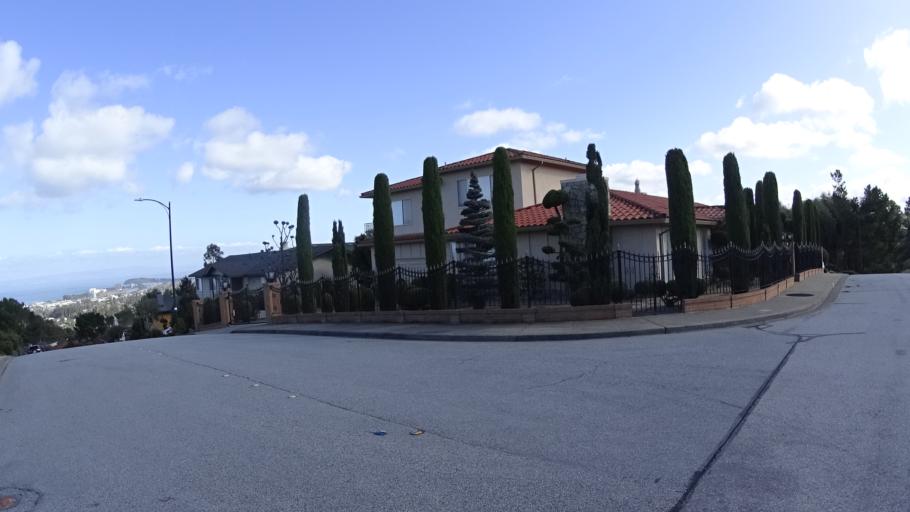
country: US
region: California
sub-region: San Mateo County
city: Millbrae
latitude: 37.5843
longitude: -122.3969
